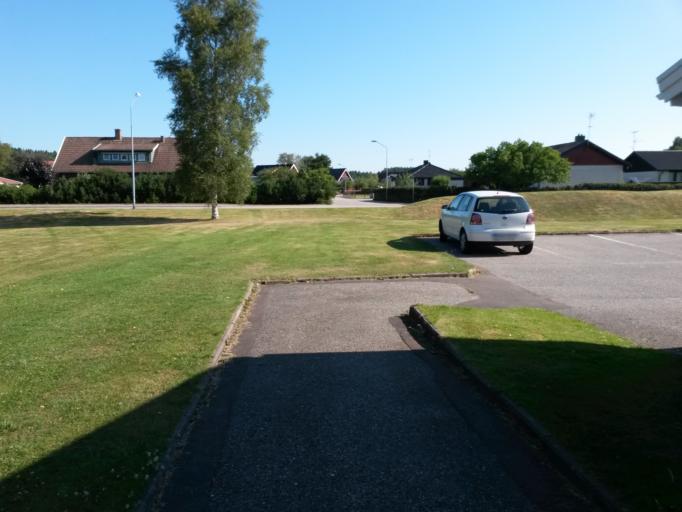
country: SE
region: Vaestra Goetaland
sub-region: Vargarda Kommun
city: Vargarda
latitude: 58.0412
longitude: 12.8146
